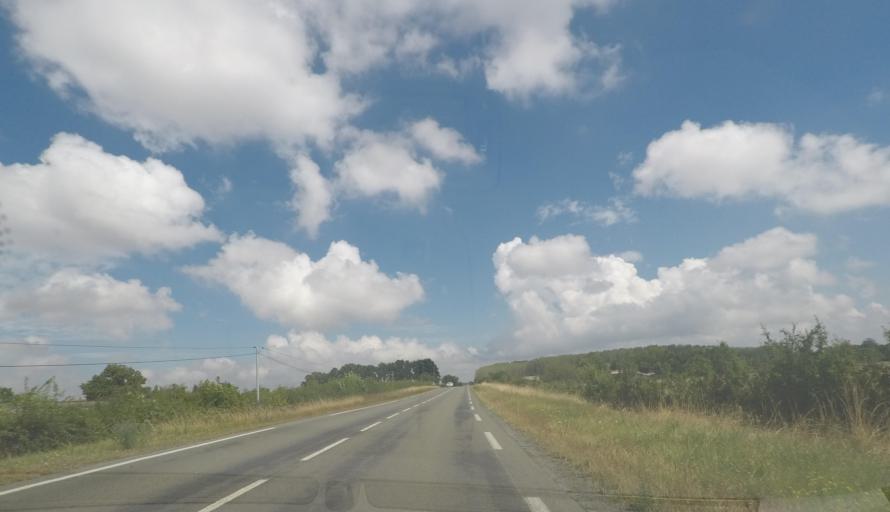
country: FR
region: Pays de la Loire
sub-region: Departement de la Sarthe
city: Saint-Cosme-en-Vairais
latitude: 48.2644
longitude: 0.4471
